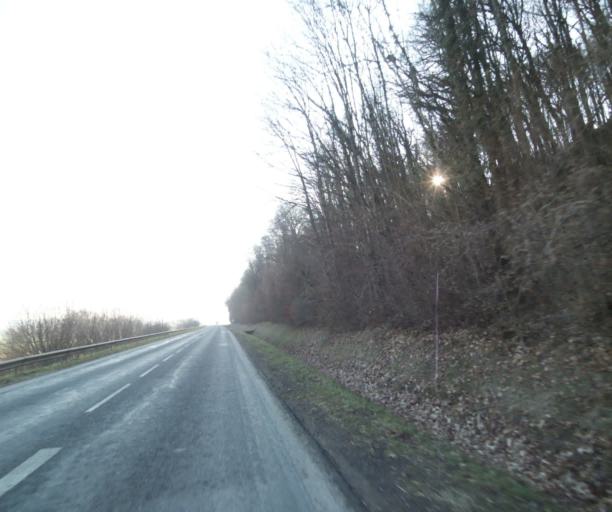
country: FR
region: Champagne-Ardenne
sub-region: Departement de la Haute-Marne
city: Chevillon
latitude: 48.5170
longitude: 5.1093
